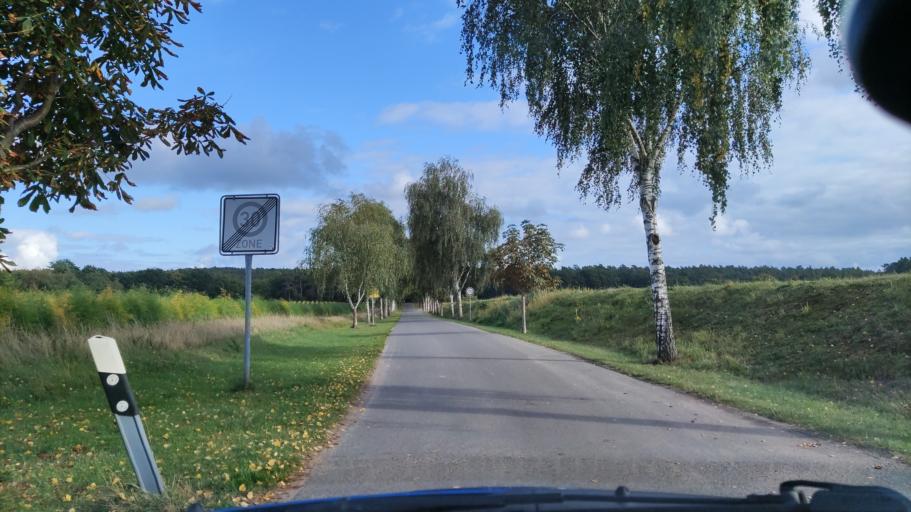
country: DE
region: Lower Saxony
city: Deutsch Evern
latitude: 53.2003
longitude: 10.4447
